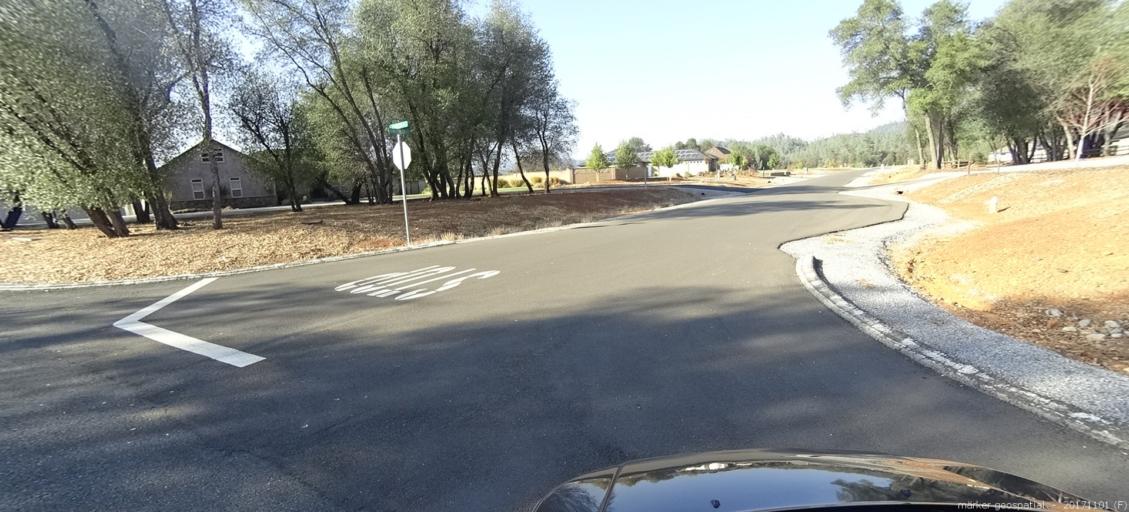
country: US
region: California
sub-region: Shasta County
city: Bella Vista
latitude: 40.6807
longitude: -122.2920
